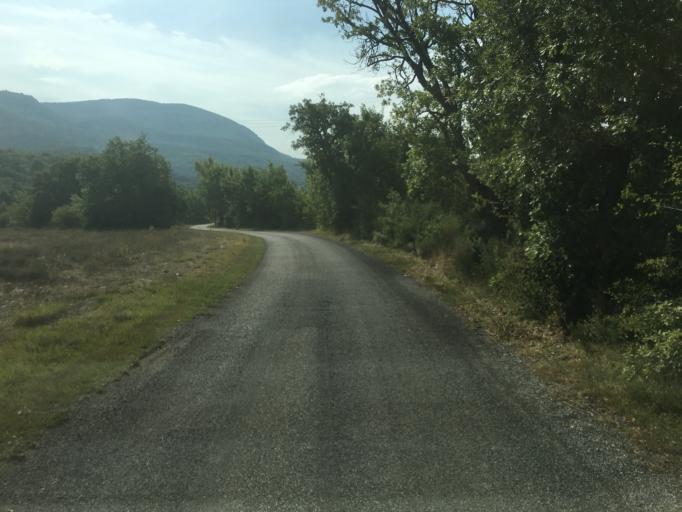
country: FR
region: Provence-Alpes-Cote d'Azur
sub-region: Departement des Alpes-de-Haute-Provence
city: Mallemoisson
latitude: 43.9386
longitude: 6.1838
